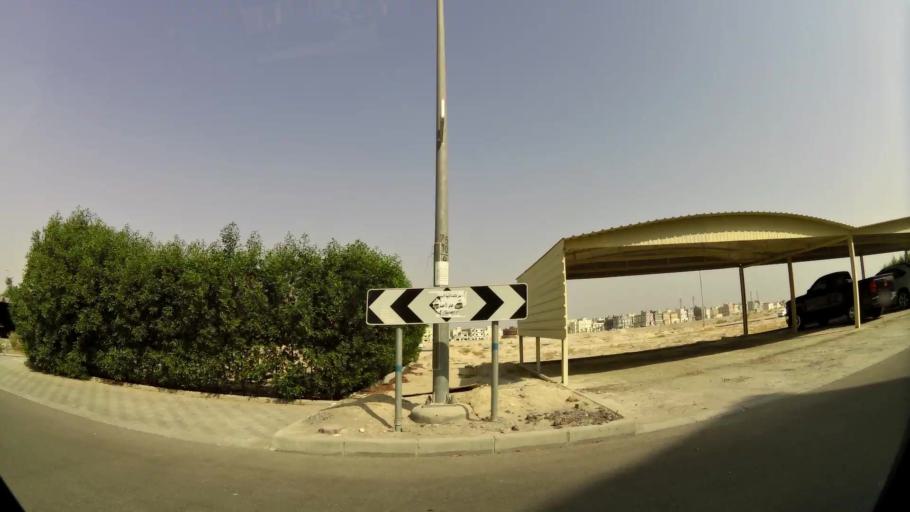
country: KW
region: Muhafazat al Jahra'
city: Al Jahra'
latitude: 29.3411
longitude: 47.7665
